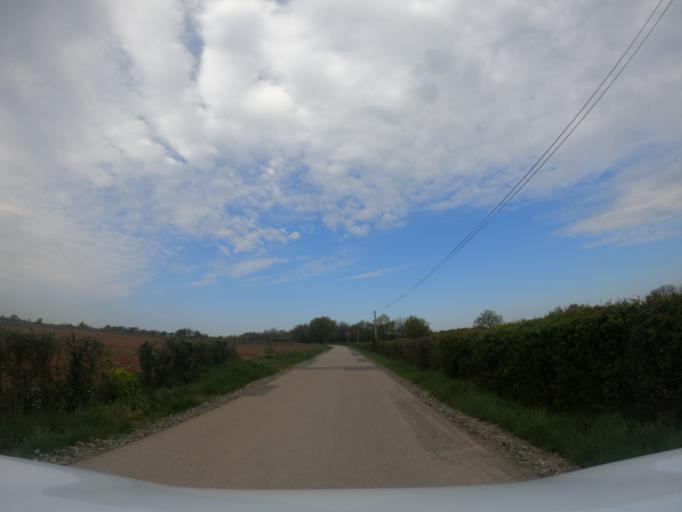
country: FR
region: Pays de la Loire
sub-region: Departement de la Vendee
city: Le Champ-Saint-Pere
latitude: 46.5331
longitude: -1.3331
